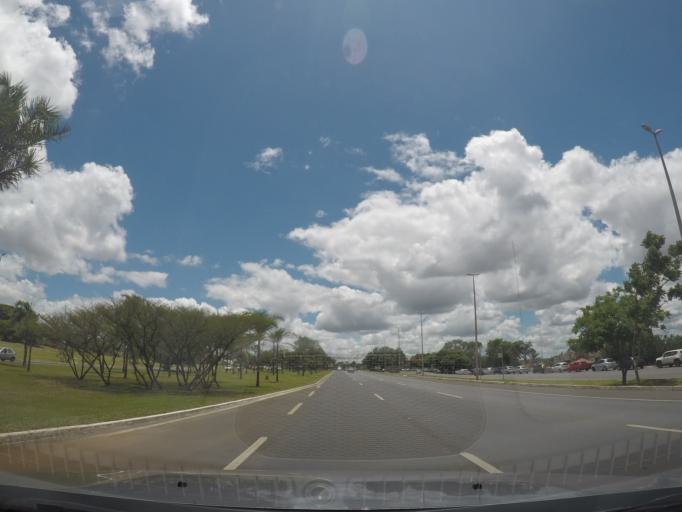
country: BR
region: Federal District
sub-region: Brasilia
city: Brasilia
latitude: -15.8436
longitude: -47.9442
